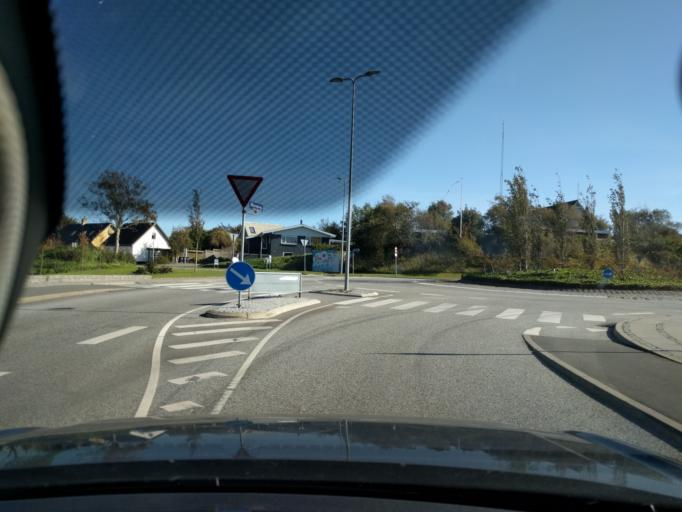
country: DK
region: North Denmark
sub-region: Vesthimmerland Kommune
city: Logstor
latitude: 56.9674
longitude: 9.2664
